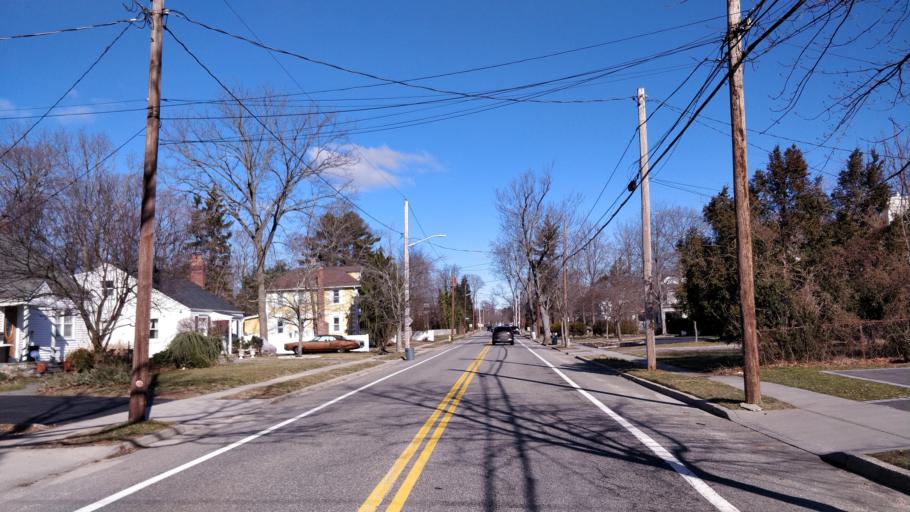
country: US
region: New York
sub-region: Suffolk County
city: Smithtown
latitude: 40.8489
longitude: -73.1976
